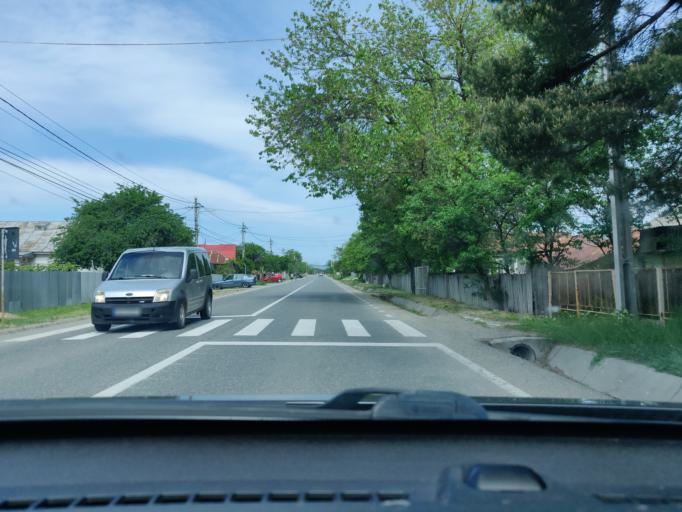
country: RO
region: Vrancea
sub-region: Comuna Bolotesti
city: Gagesti
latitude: 45.8759
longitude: 27.0325
